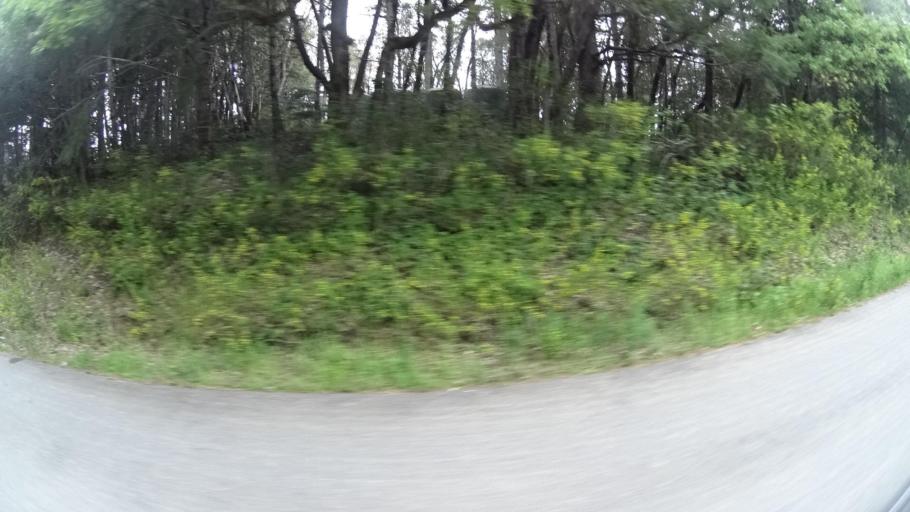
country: US
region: California
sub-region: Humboldt County
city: Redway
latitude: 40.2934
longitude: -123.8175
